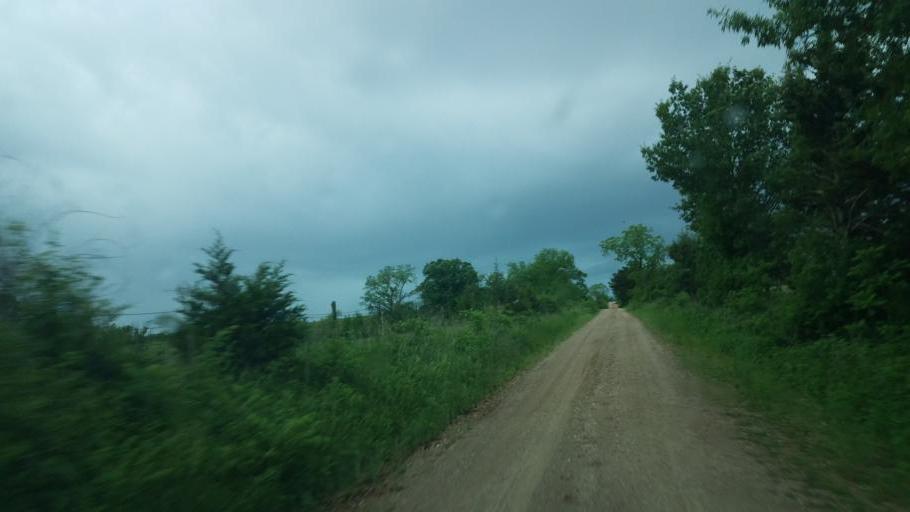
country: US
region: Missouri
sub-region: Moniteau County
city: California
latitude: 38.7503
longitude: -92.6219
